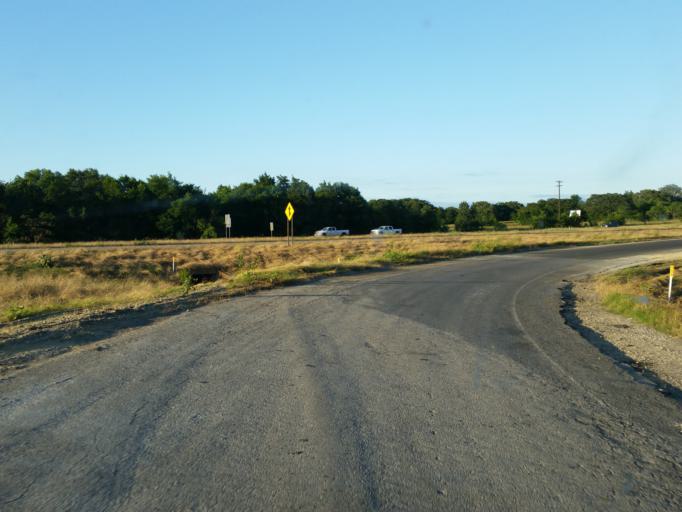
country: US
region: Texas
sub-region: Van Zandt County
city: Wills Point
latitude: 32.6675
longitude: -96.1447
